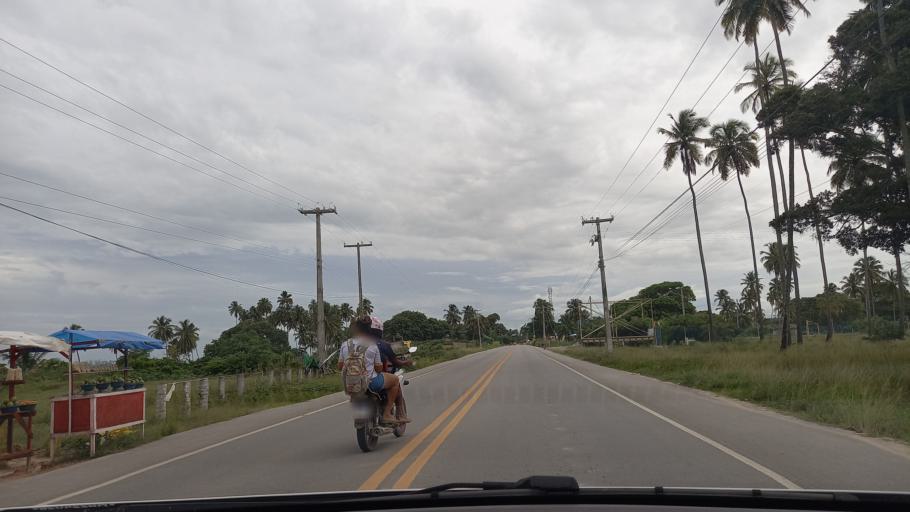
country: BR
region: Pernambuco
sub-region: Sao Jose Da Coroa Grande
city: Sao Jose da Coroa Grande
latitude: -8.9213
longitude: -35.1576
